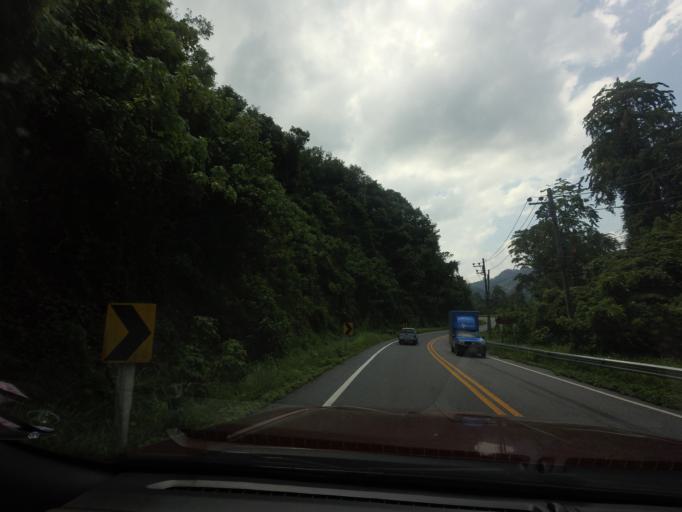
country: TH
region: Yala
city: Than To
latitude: 6.0341
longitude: 101.1964
